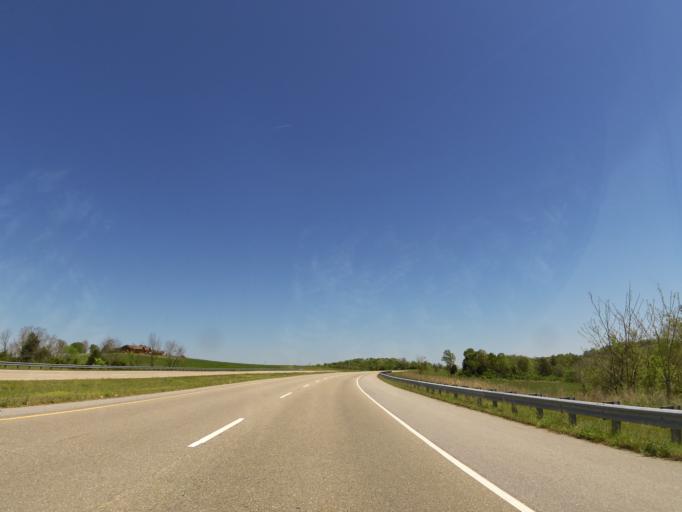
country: US
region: Tennessee
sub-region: Greene County
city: Mosheim
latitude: 36.0333
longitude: -83.0278
